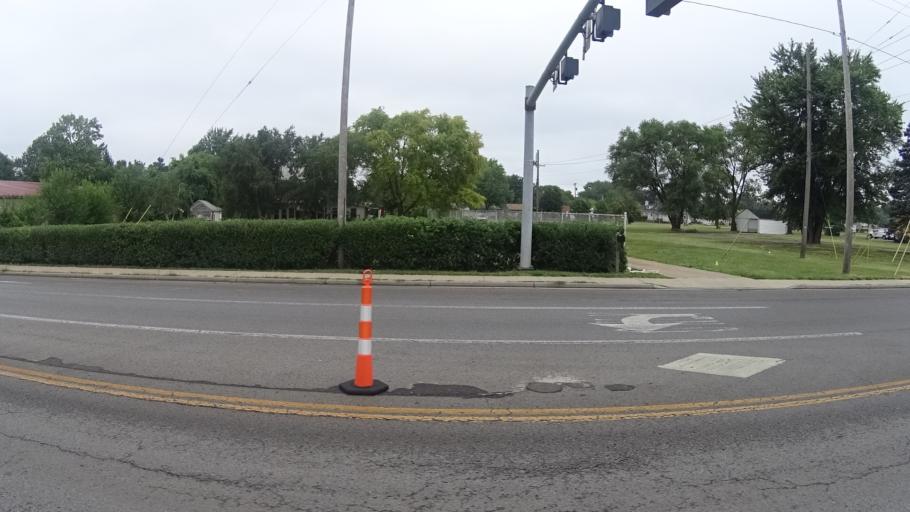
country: US
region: Ohio
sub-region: Erie County
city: Sandusky
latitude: 41.4427
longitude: -82.6879
